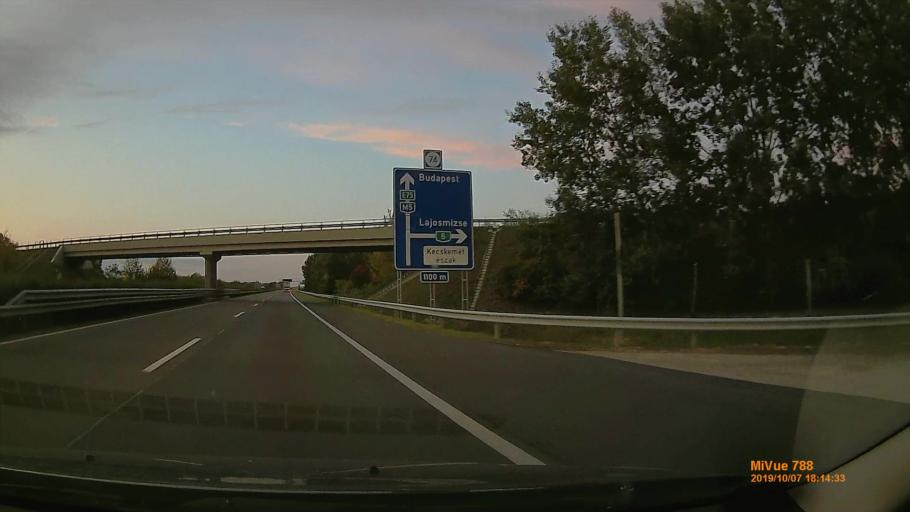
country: HU
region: Bacs-Kiskun
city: Lajosmizse
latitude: 46.9746
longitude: 19.6132
